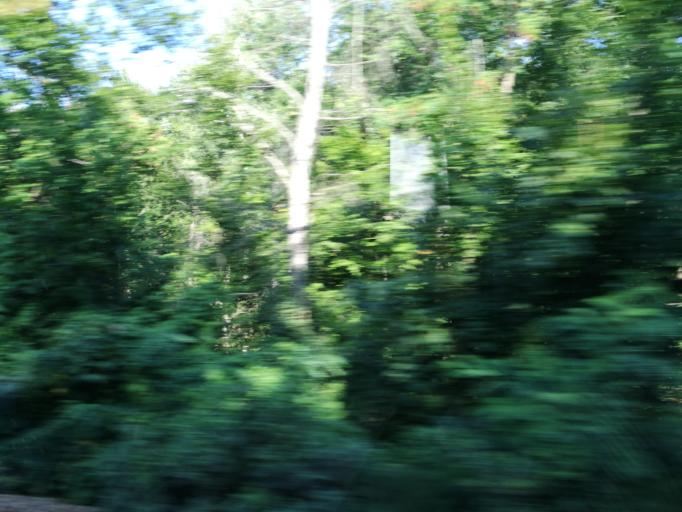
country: RO
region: Iasi
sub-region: Comuna Ciurea
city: Ciurea
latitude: 47.0233
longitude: 27.5820
